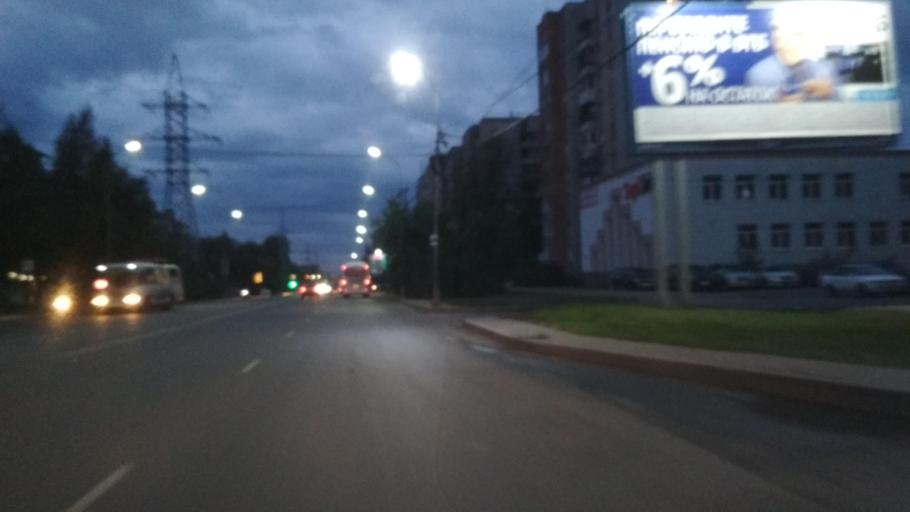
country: RU
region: Tomsk
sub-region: Tomskiy Rayon
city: Tomsk
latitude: 56.4651
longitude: 84.9943
